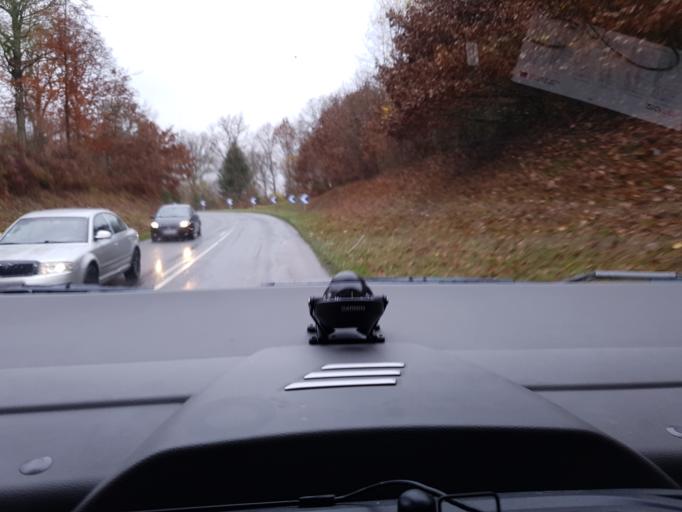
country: FR
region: Haute-Normandie
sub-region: Departement de l'Eure
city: Pont-Saint-Pierre
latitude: 49.3266
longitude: 1.2919
